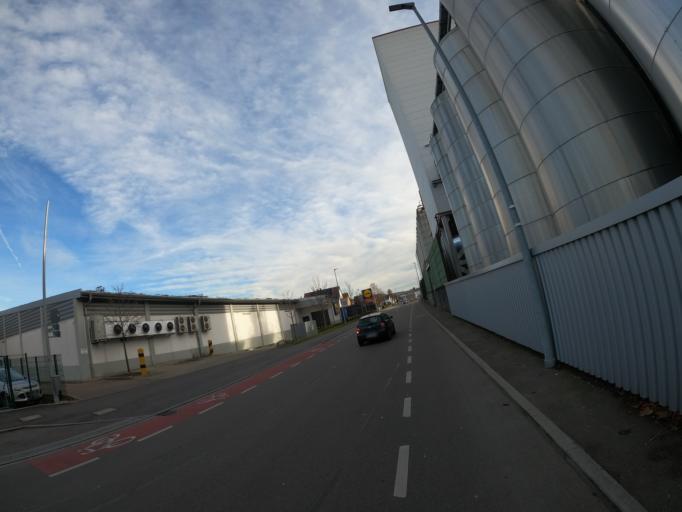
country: DE
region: Baden-Wuerttemberg
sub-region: Regierungsbezirk Stuttgart
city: Eislingen
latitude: 48.6965
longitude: 9.7103
